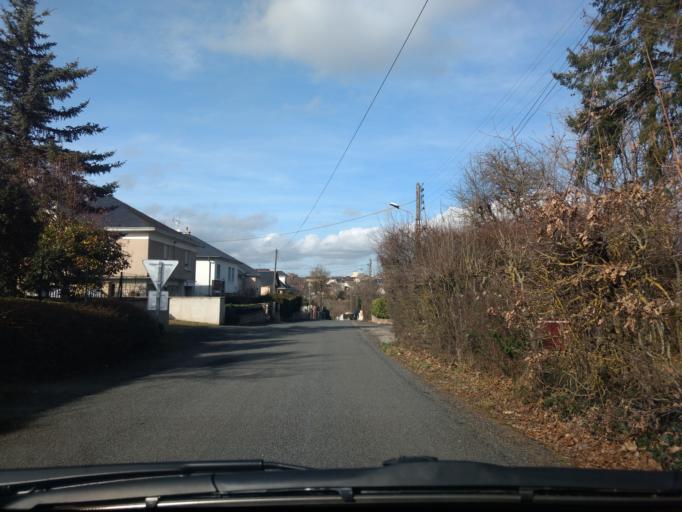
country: FR
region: Midi-Pyrenees
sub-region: Departement de l'Aveyron
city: Naucelle
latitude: 44.1924
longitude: 2.3435
